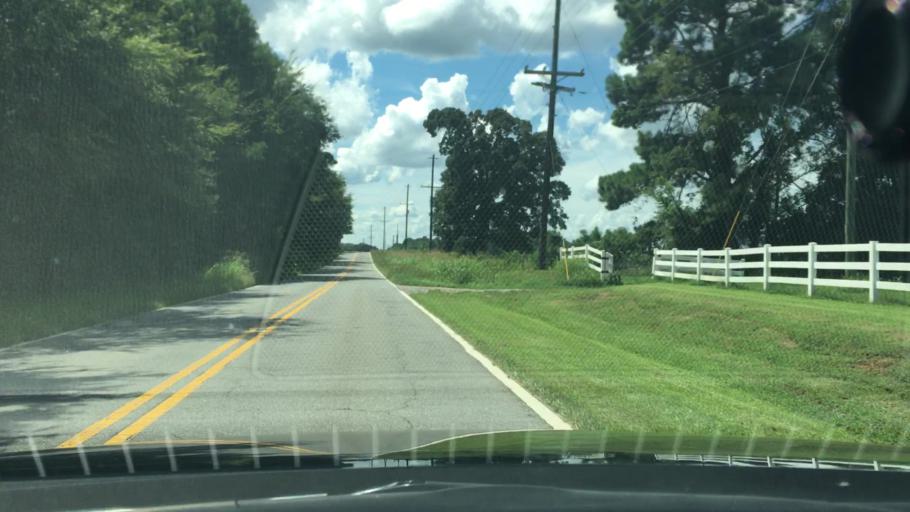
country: US
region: Georgia
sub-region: Putnam County
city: Jefferson
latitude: 33.3651
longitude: -83.2723
